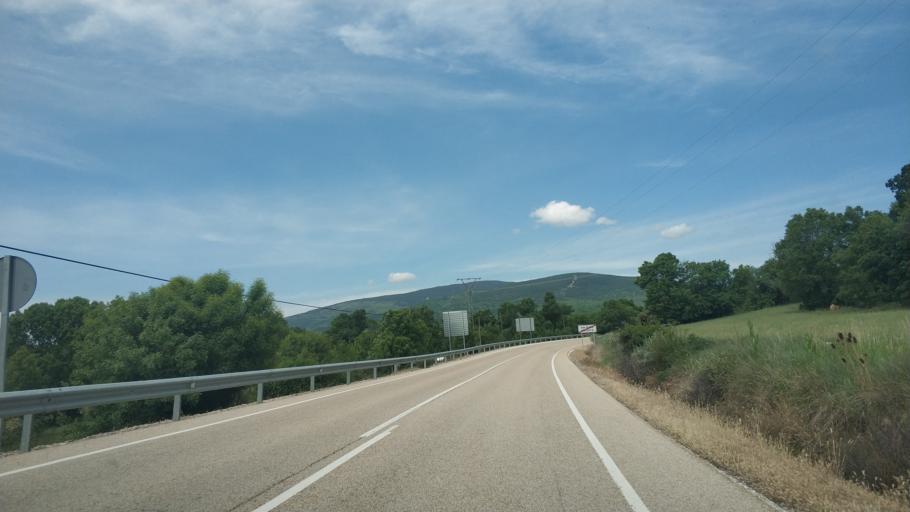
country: ES
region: Castille and Leon
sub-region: Provincia de Soria
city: Sotillo del Rincon
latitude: 41.8924
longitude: -2.6345
